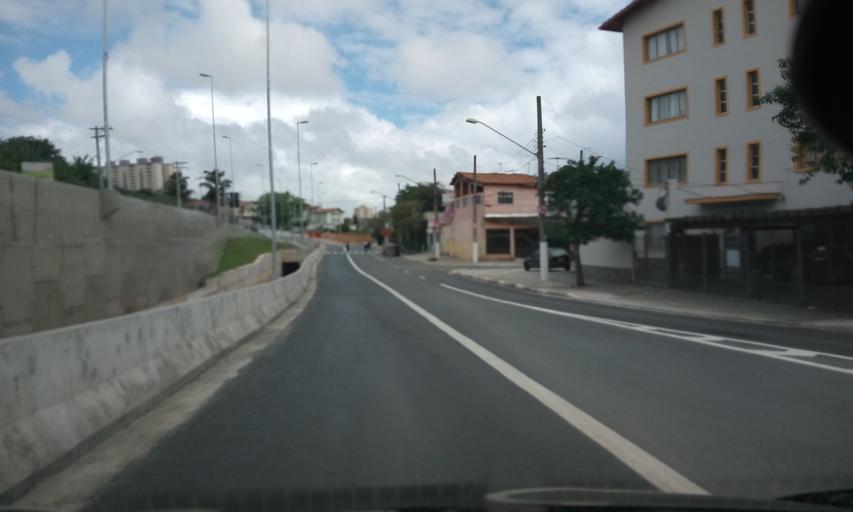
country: BR
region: Sao Paulo
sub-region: Sao Bernardo Do Campo
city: Sao Bernardo do Campo
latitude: -23.7104
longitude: -46.5873
